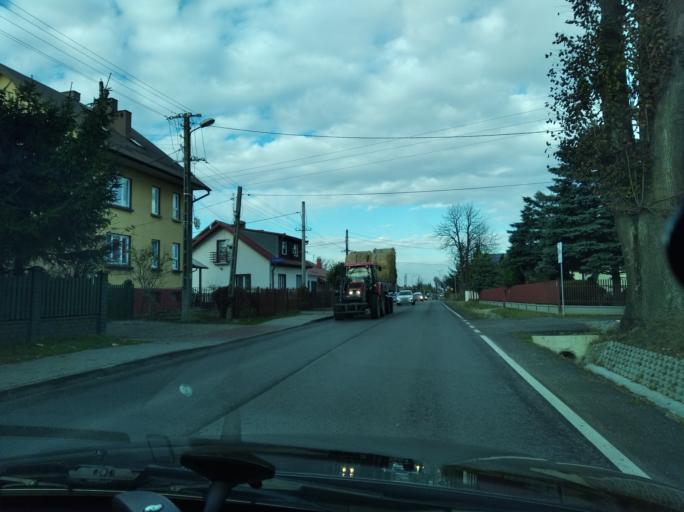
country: PL
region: Subcarpathian Voivodeship
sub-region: Powiat debicki
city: Debica
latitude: 50.0408
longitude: 21.4345
